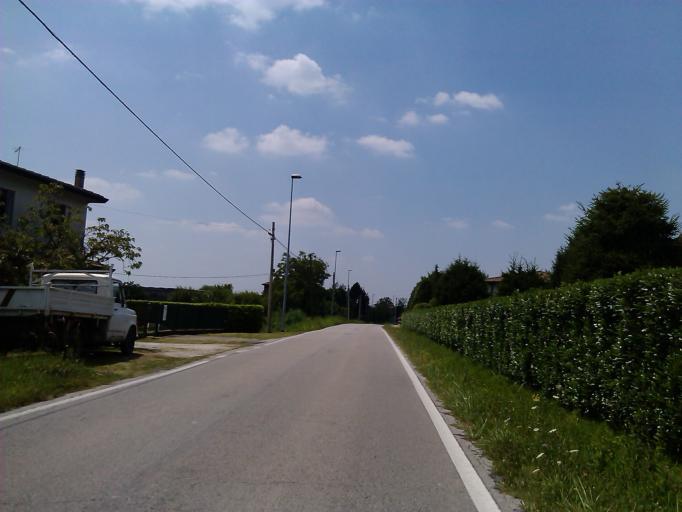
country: IT
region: Veneto
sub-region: Provincia di Venezia
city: Fiesso
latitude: 45.4131
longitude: 12.0425
